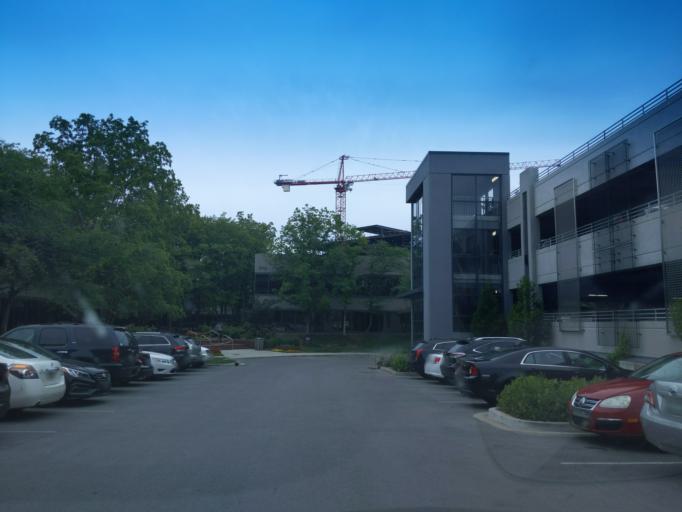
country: US
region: Tennessee
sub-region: Williamson County
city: Brentwood
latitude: 36.0422
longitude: -86.7737
